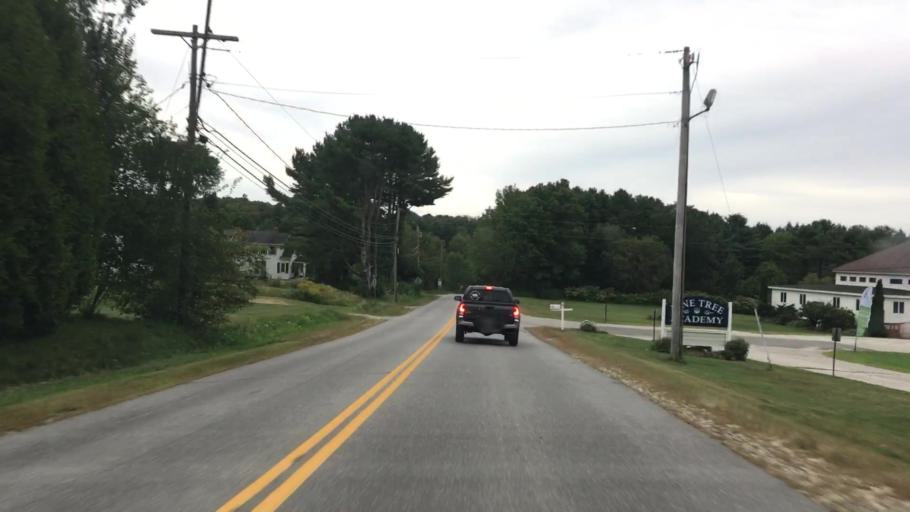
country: US
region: Maine
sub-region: Cumberland County
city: Freeport
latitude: 43.8637
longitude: -70.1145
